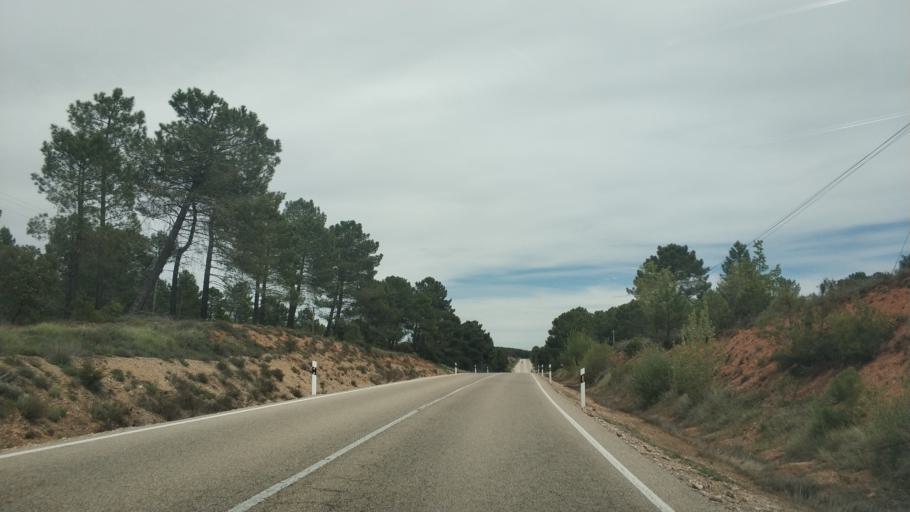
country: ES
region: Castille and Leon
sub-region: Provincia de Soria
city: Valdenebro
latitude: 41.5629
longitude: -2.9807
